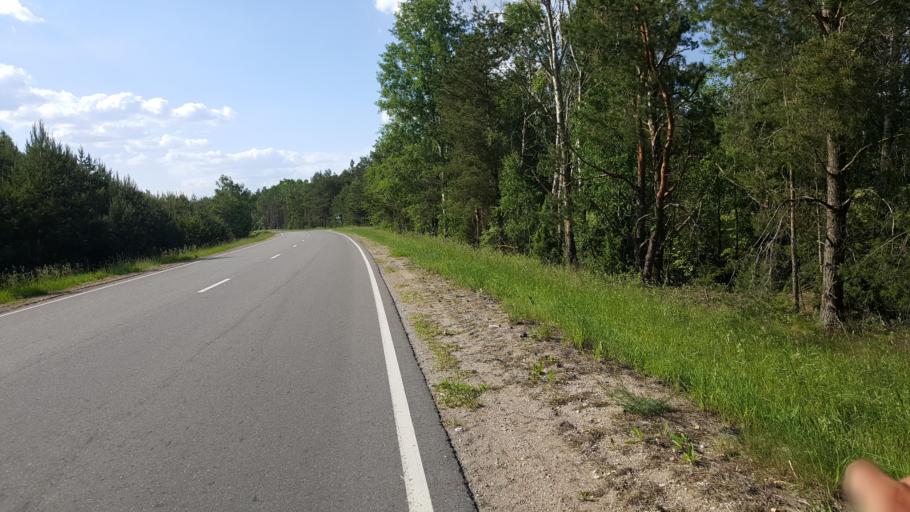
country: BY
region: Brest
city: Zhabinka
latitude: 52.3708
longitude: 24.1391
